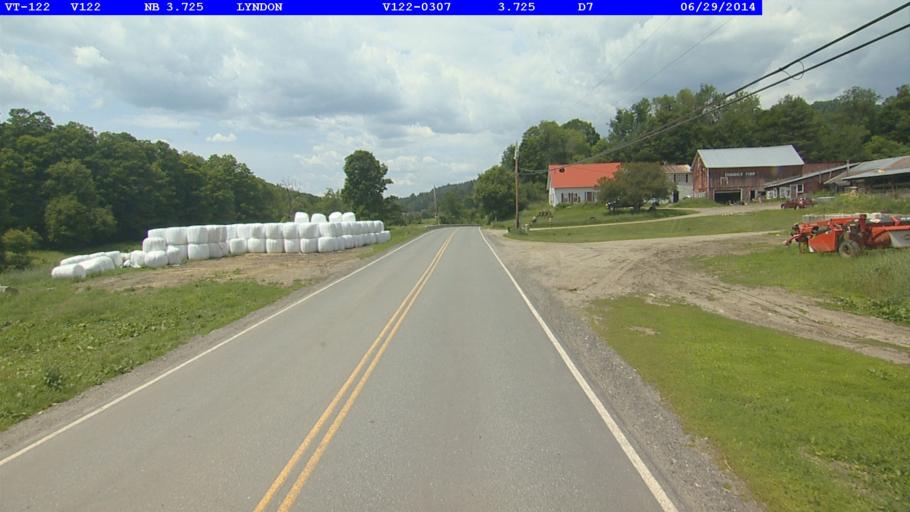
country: US
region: Vermont
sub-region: Caledonia County
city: Lyndonville
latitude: 44.5745
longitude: -72.0528
